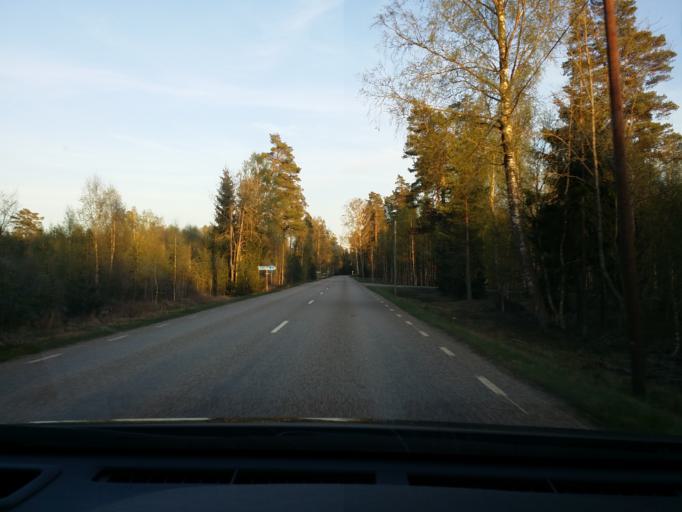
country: SE
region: Vaestmanland
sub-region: Sala Kommun
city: Sala
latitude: 59.8281
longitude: 16.5179
